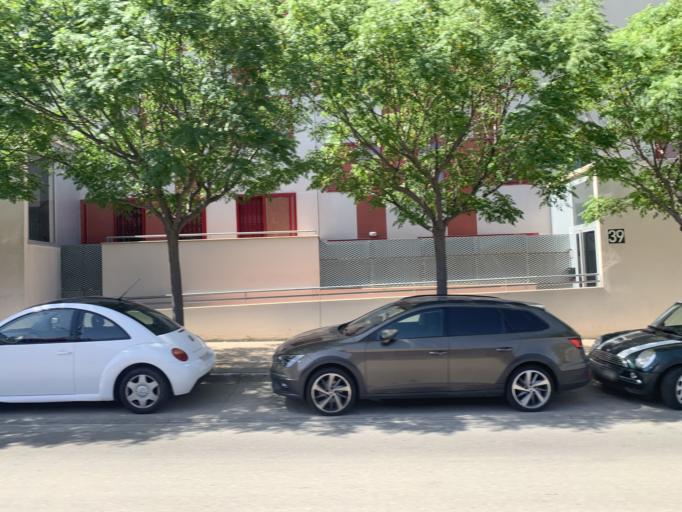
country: ES
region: Aragon
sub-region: Provincia de Zaragoza
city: Montecanal
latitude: 41.6231
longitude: -0.9314
